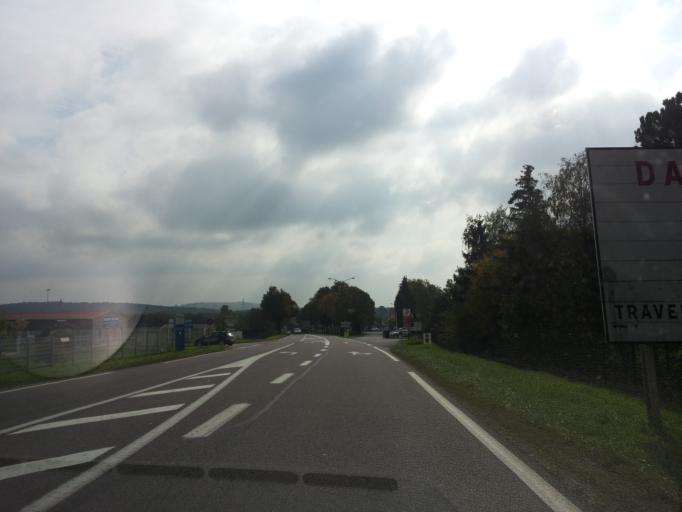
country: FR
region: Lorraine
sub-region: Departement de la Moselle
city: Solgne
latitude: 48.9716
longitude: 6.2953
